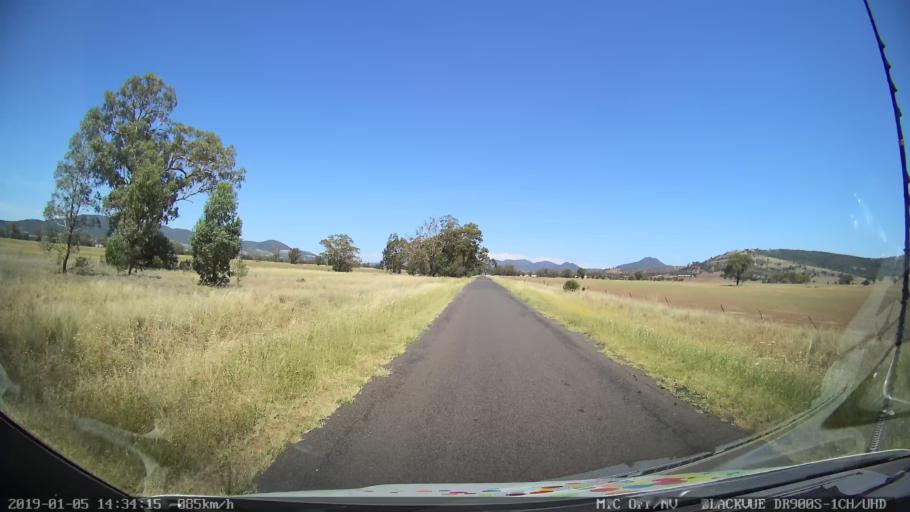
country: AU
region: New South Wales
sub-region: Tamworth Municipality
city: Phillip
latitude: -31.2314
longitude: 150.6394
